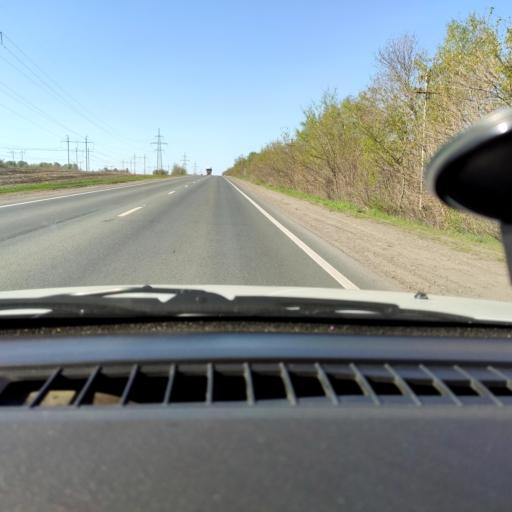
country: RU
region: Samara
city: Dubovyy Umet
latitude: 53.0805
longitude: 50.3895
